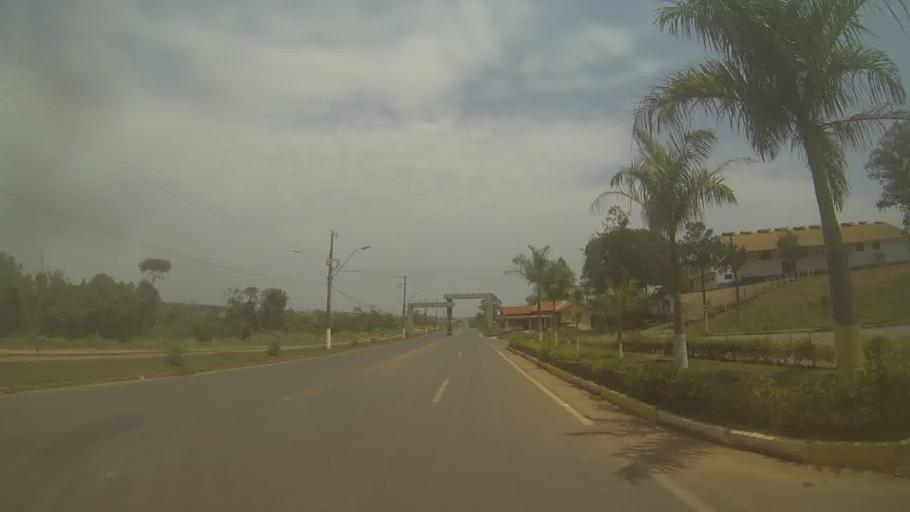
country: BR
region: Minas Gerais
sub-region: Bambui
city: Bambui
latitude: -20.0140
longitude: -45.9506
